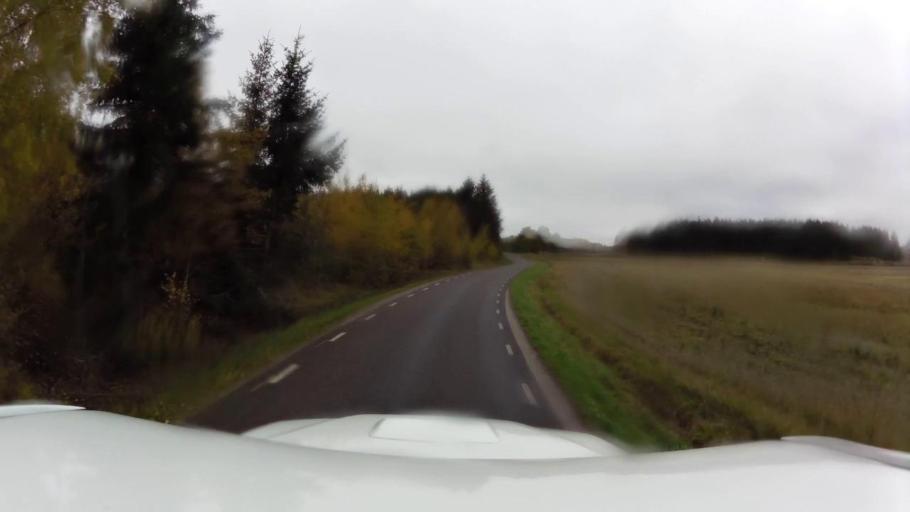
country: SE
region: OEstergoetland
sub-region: Linkopings Kommun
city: Linghem
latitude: 58.4666
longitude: 15.7850
